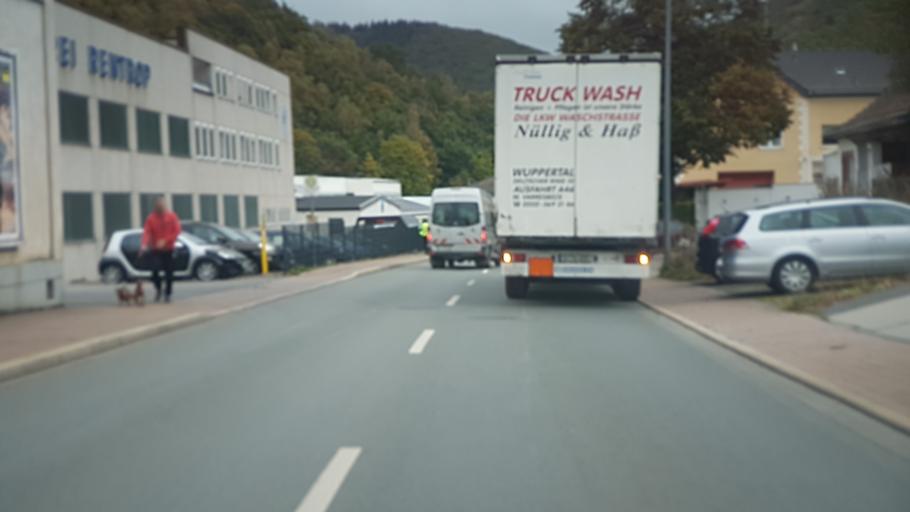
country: DE
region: North Rhine-Westphalia
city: Plettenberg
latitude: 51.1729
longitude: 7.8542
